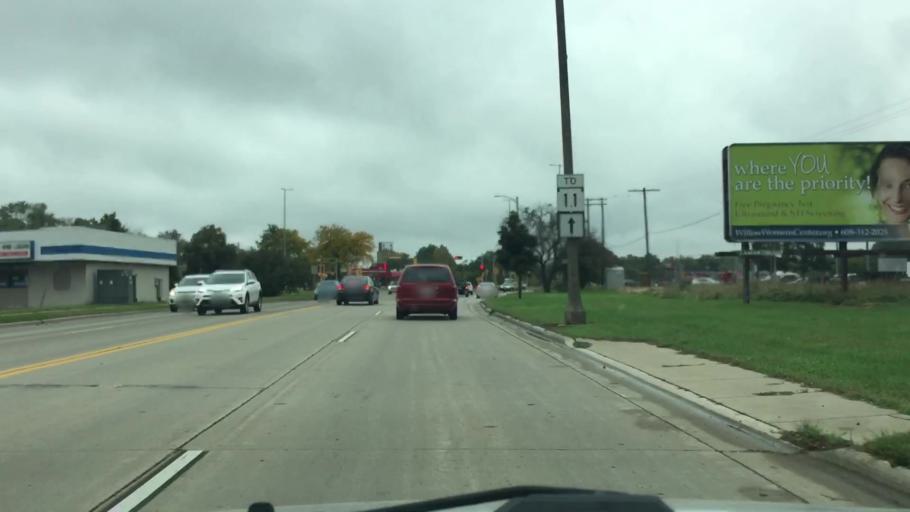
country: US
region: Wisconsin
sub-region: Rock County
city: Janesville
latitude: 42.6806
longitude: -89.0309
